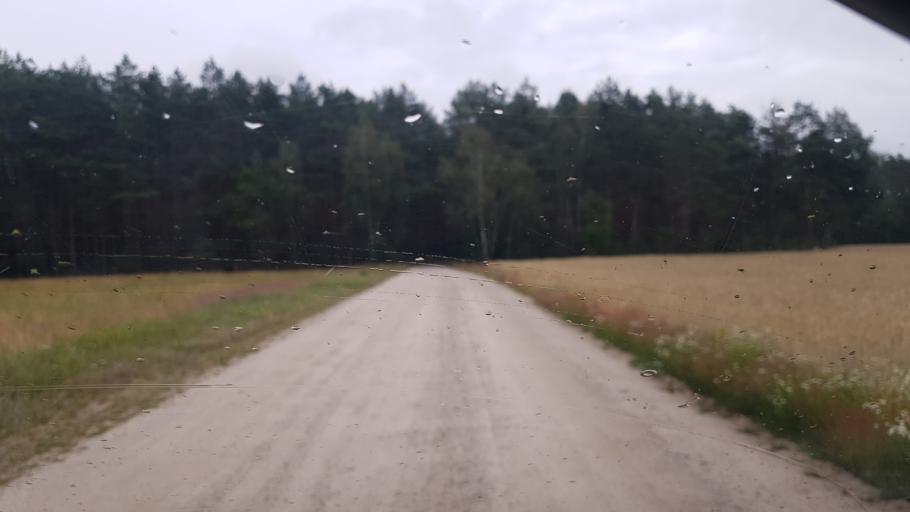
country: DE
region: Brandenburg
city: Finsterwalde
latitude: 51.5893
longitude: 13.7203
